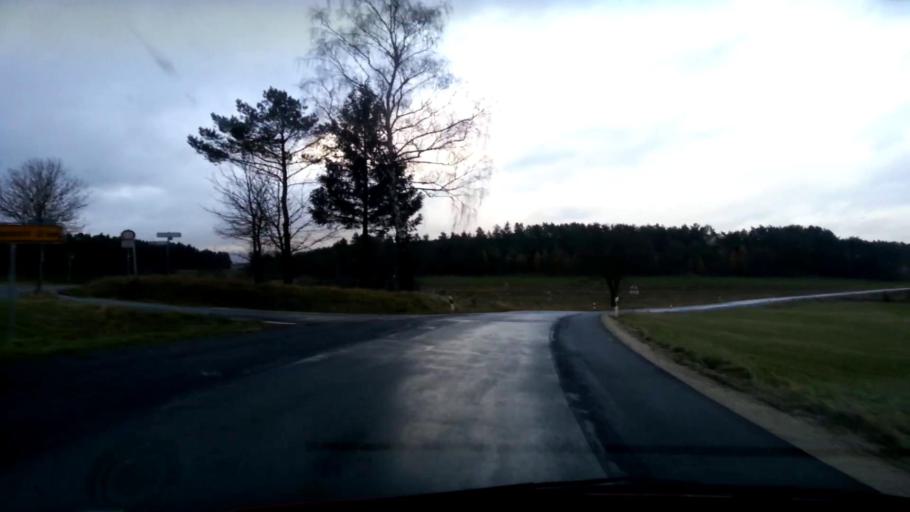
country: DE
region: Bavaria
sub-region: Upper Franconia
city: Poxdorf
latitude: 49.9239
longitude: 11.1303
